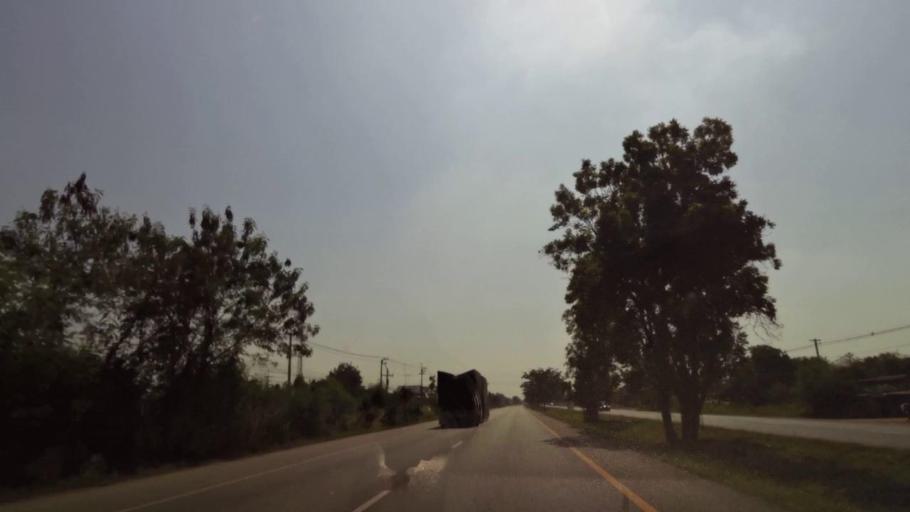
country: TH
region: Phichit
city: Bueng Na Rang
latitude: 16.3094
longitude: 100.1286
